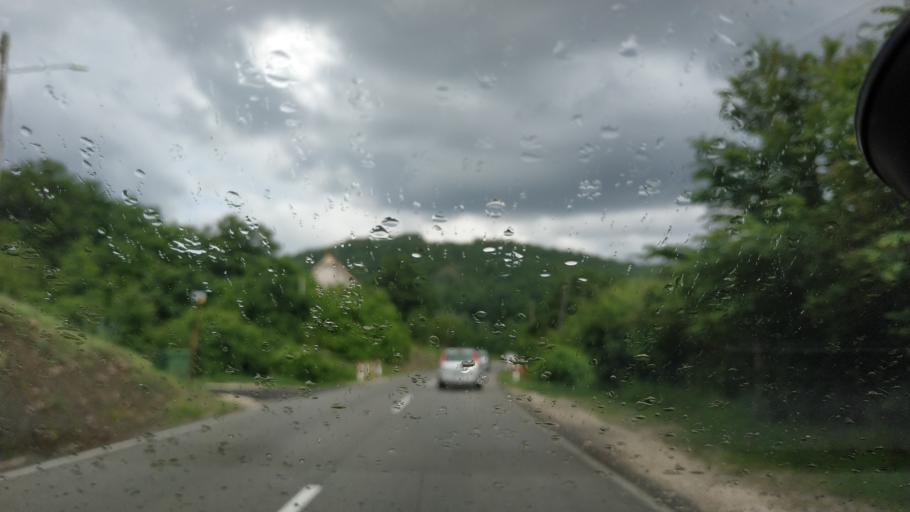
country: RS
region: Central Serbia
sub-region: Borski Okrug
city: Bor
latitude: 44.0573
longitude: 22.0564
